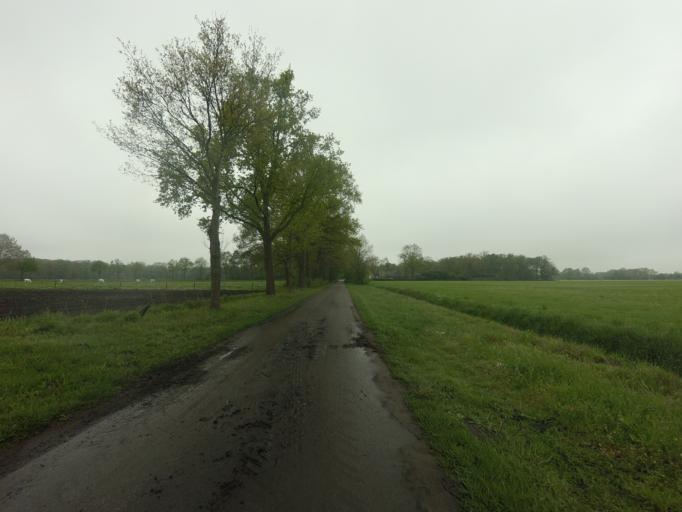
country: DE
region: North Rhine-Westphalia
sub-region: Regierungsbezirk Munster
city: Vreden
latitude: 52.1302
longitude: 6.8504
